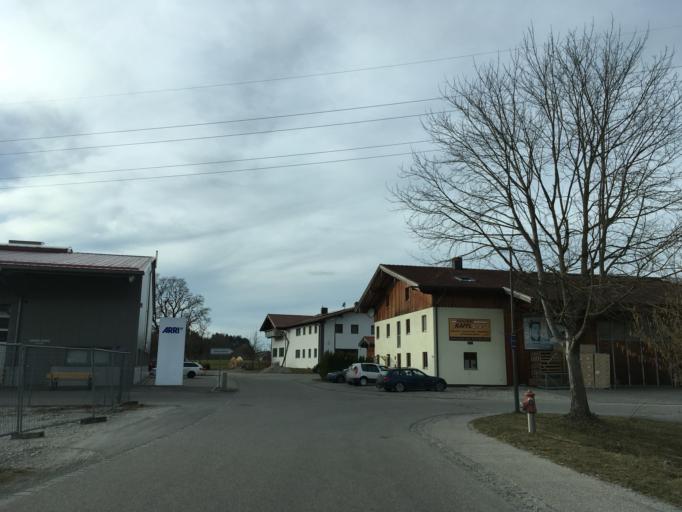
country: DE
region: Bavaria
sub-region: Upper Bavaria
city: Prutting
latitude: 47.8981
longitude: 12.2027
